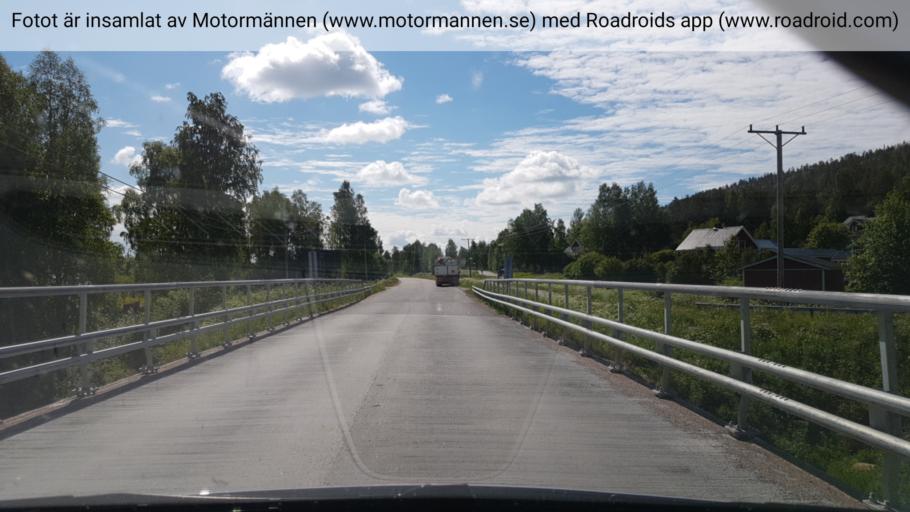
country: FI
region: Lapland
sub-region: Torniolaakso
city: Pello
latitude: 66.6584
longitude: 23.8530
